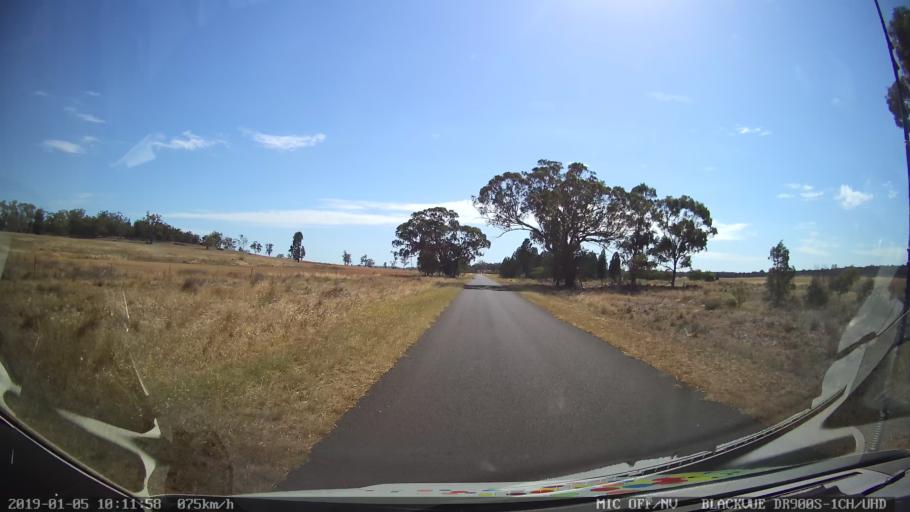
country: AU
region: New South Wales
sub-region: Gilgandra
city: Gilgandra
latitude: -31.6104
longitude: 148.9075
